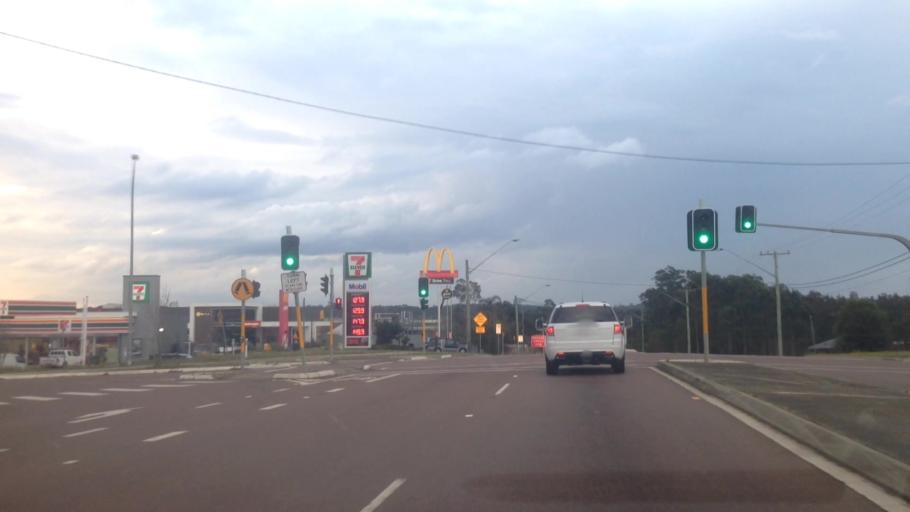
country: AU
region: New South Wales
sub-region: Wyong Shire
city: Tuggerawong
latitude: -33.2657
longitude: 151.4550
